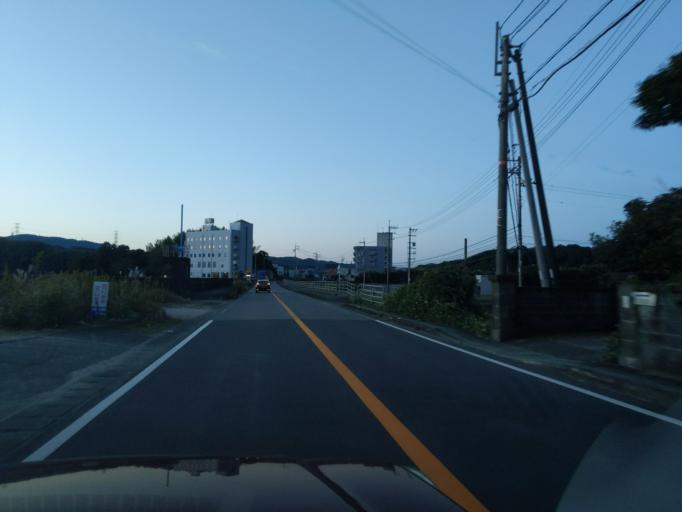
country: JP
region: Tokushima
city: Anan
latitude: 33.8659
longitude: 134.6322
